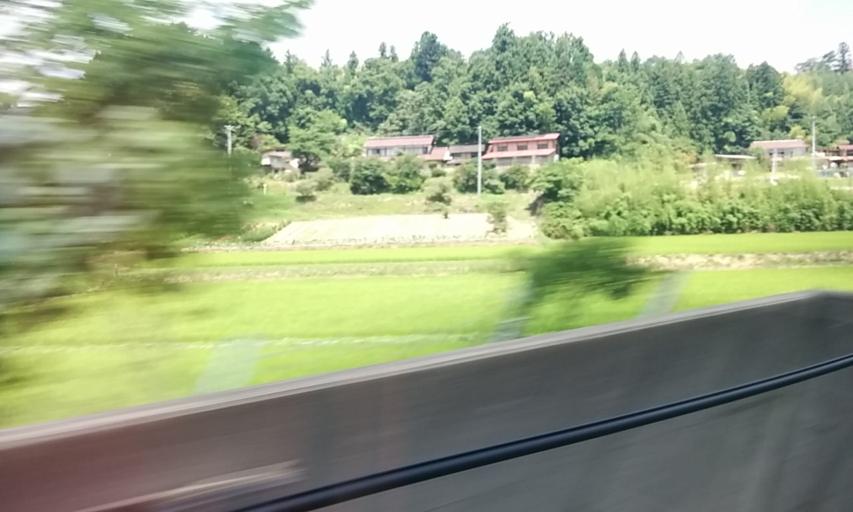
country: JP
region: Fukushima
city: Nihommatsu
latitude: 37.5849
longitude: 140.4683
